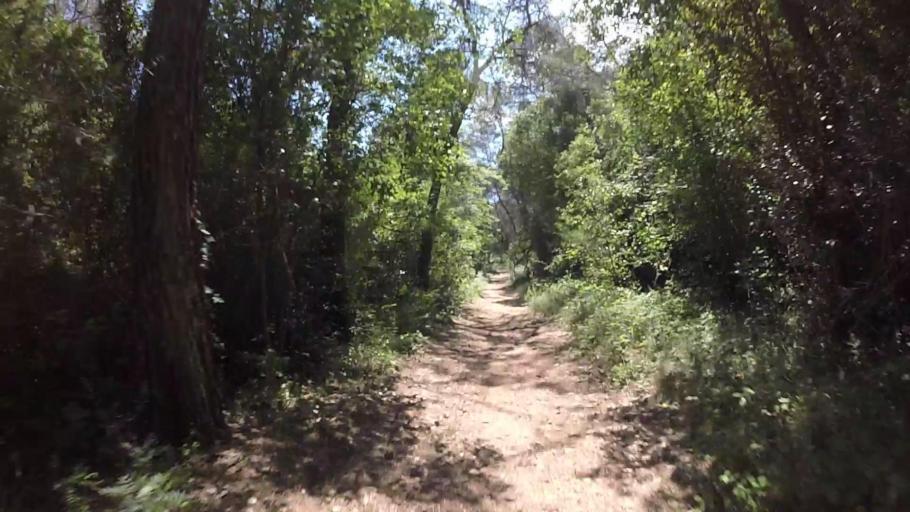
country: FR
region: Provence-Alpes-Cote d'Azur
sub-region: Departement des Alpes-Maritimes
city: Mougins
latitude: 43.5961
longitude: 7.0194
